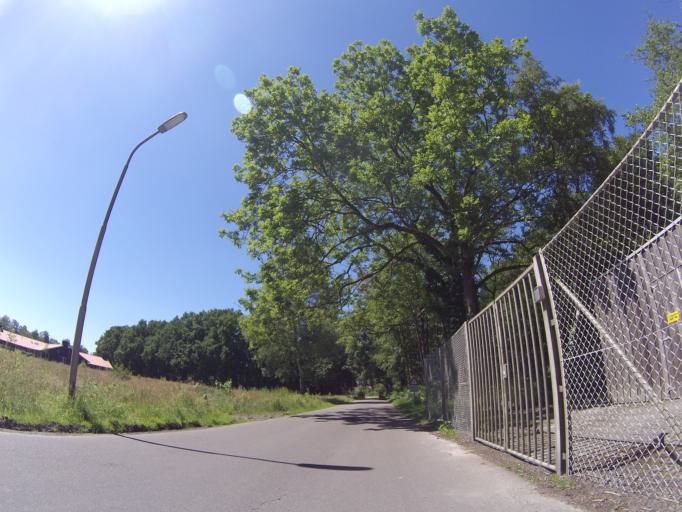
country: NL
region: Drenthe
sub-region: Gemeente Assen
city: Assen
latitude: 52.9797
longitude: 6.5684
